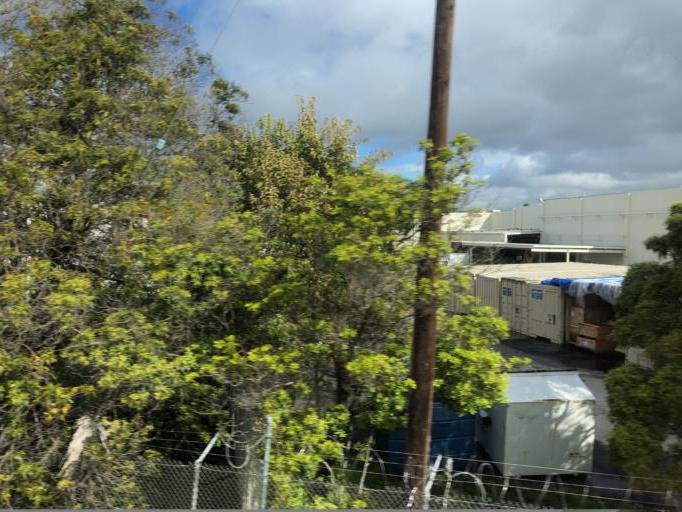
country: US
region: California
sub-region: Santa Clara County
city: Santa Clara
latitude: 37.3628
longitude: -121.9579
